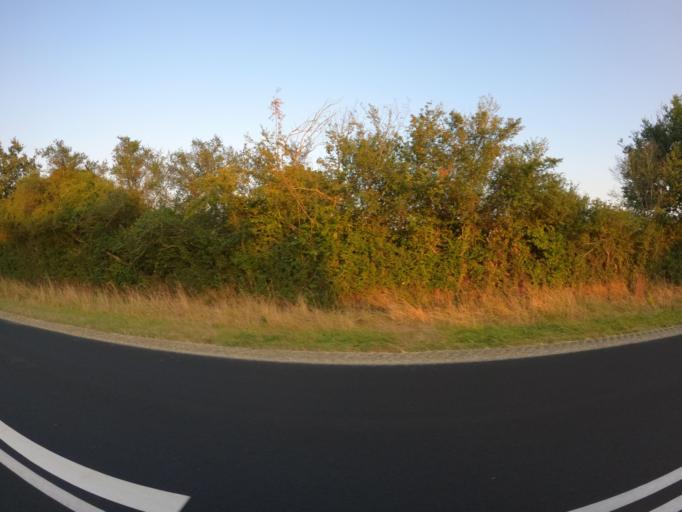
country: FR
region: Pays de la Loire
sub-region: Departement de la Sarthe
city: Auvers-le-Hamon
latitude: 47.8720
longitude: -0.4020
